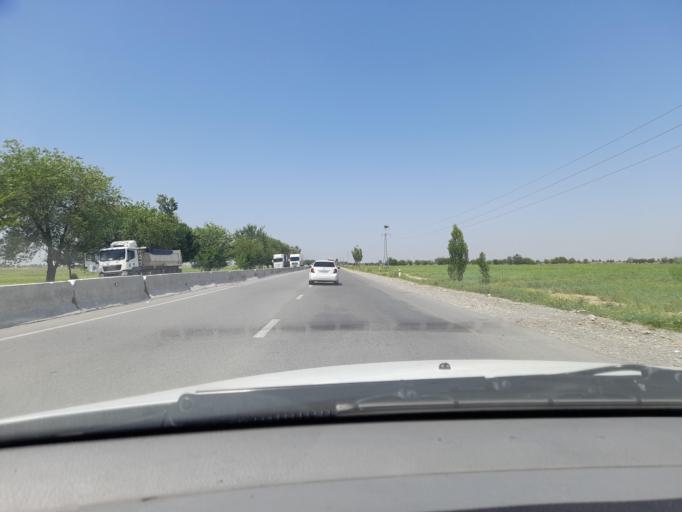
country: KZ
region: Ongtustik Qazaqstan
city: Myrzakent
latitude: 40.5556
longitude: 68.3926
